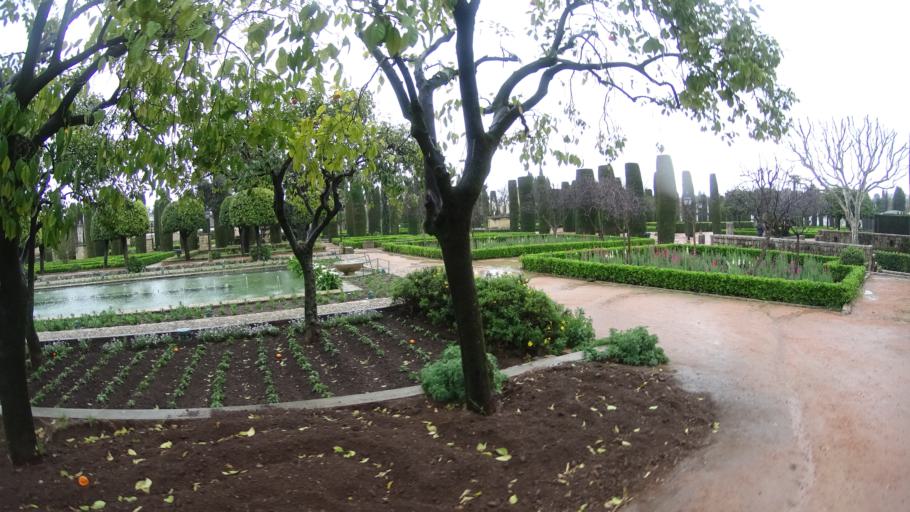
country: ES
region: Andalusia
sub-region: Province of Cordoba
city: Cordoba
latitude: 37.8756
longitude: -4.7833
